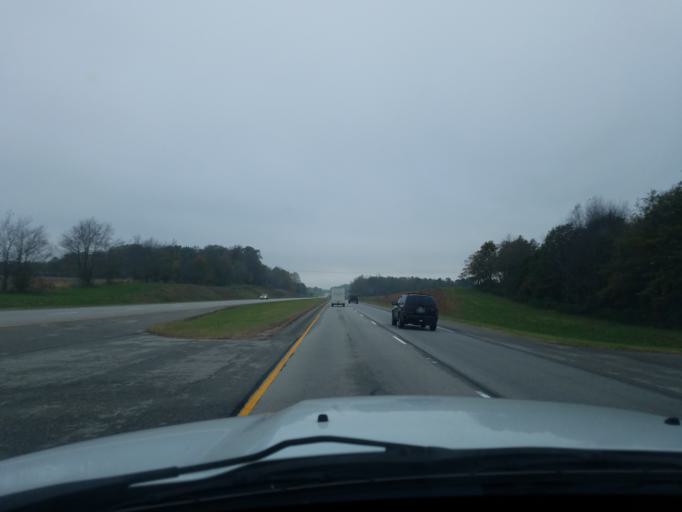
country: US
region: Kentucky
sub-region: Larue County
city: Hodgenville
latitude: 37.6181
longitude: -85.8087
